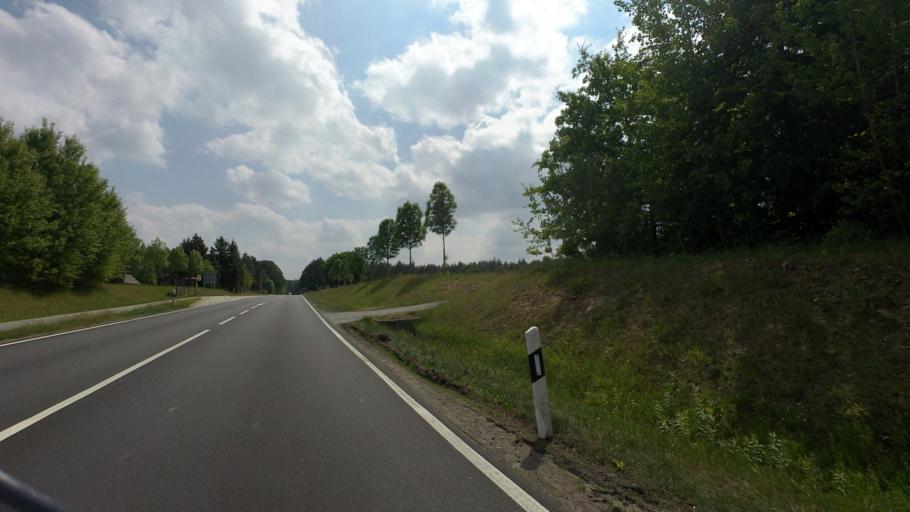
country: DE
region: Saxony
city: Rietschen
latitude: 51.3512
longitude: 14.8030
